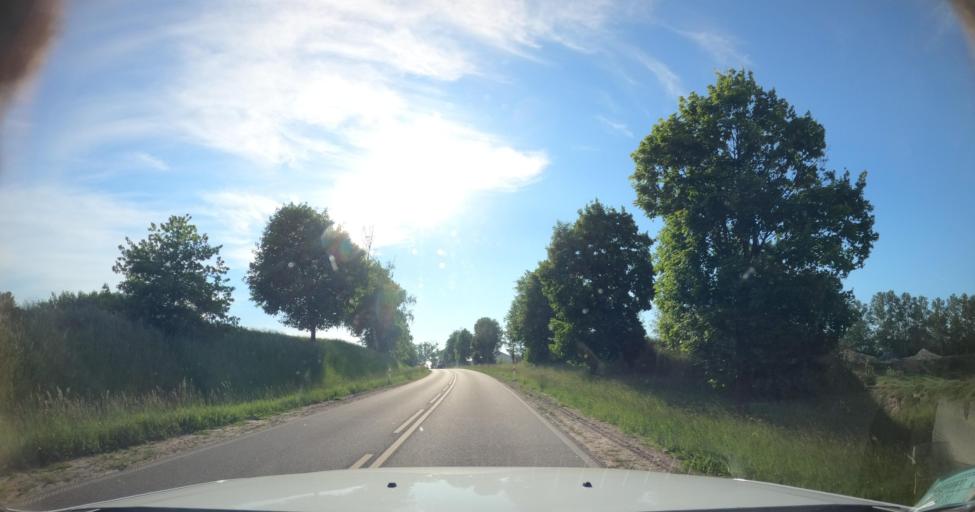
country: PL
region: Warmian-Masurian Voivodeship
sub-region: Powiat elblaski
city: Paslek
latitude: 54.0758
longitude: 19.6802
